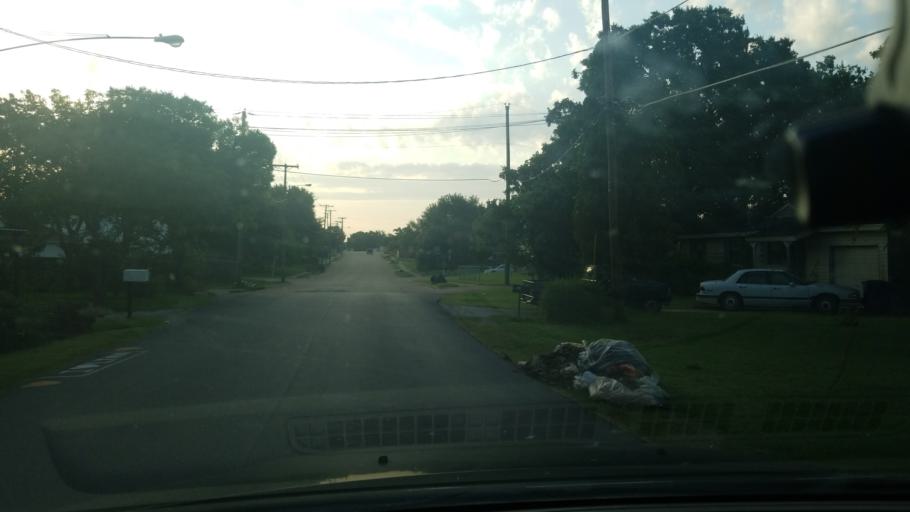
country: US
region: Texas
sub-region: Dallas County
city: Balch Springs
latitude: 32.7277
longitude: -96.6546
